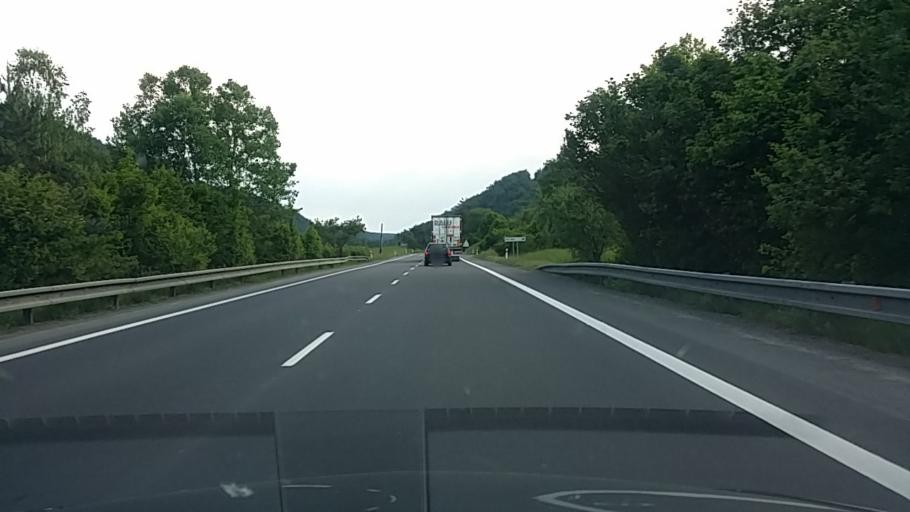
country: SK
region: Banskobystricky
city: Krupina
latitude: 48.4185
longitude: 19.0879
